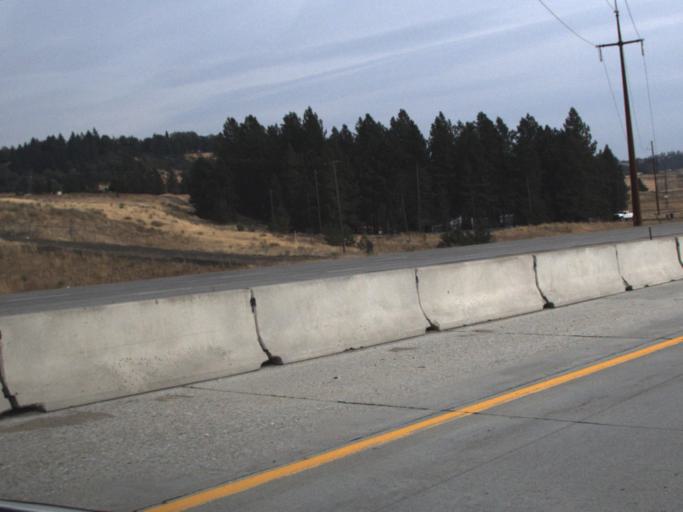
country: US
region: Washington
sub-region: Spokane County
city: Mead
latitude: 47.7331
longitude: -117.3571
